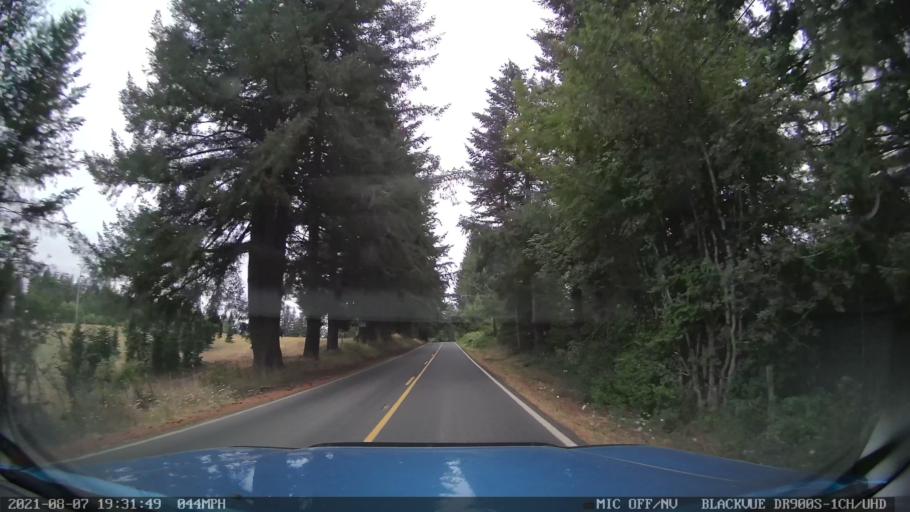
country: US
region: Oregon
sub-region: Linn County
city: Lyons
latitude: 44.8948
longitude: -122.6374
